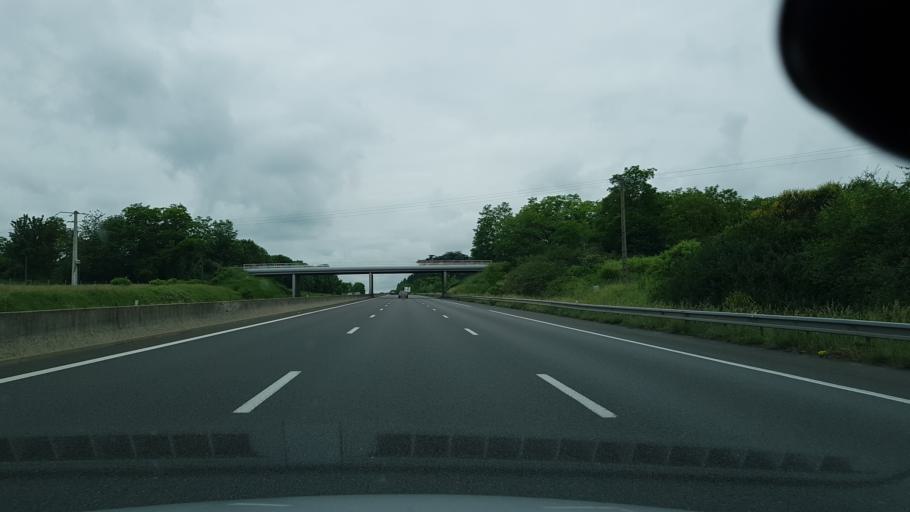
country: FR
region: Centre
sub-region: Departement du Loir-et-Cher
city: Saint-Sulpice-de-Pommeray
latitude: 47.6191
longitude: 1.2504
